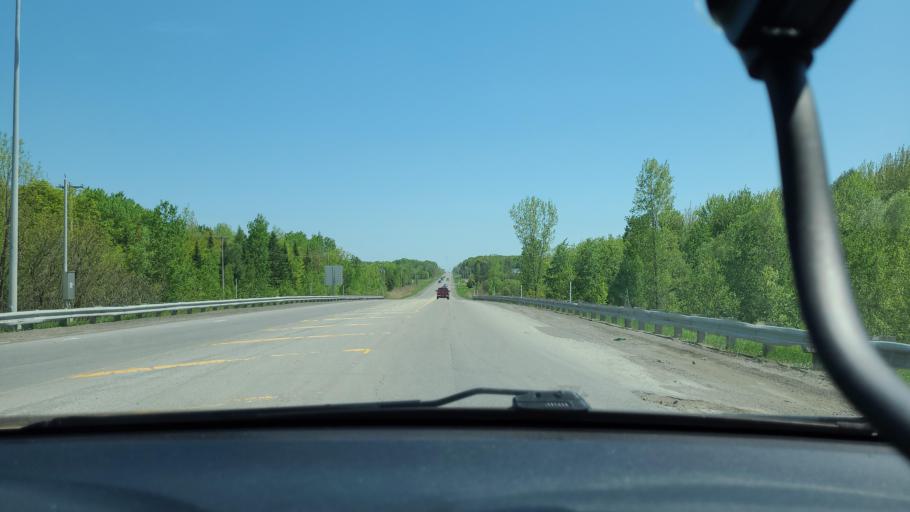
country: CA
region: Quebec
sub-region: Laurentides
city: Saint-Colomban
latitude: 45.6745
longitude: -74.1831
